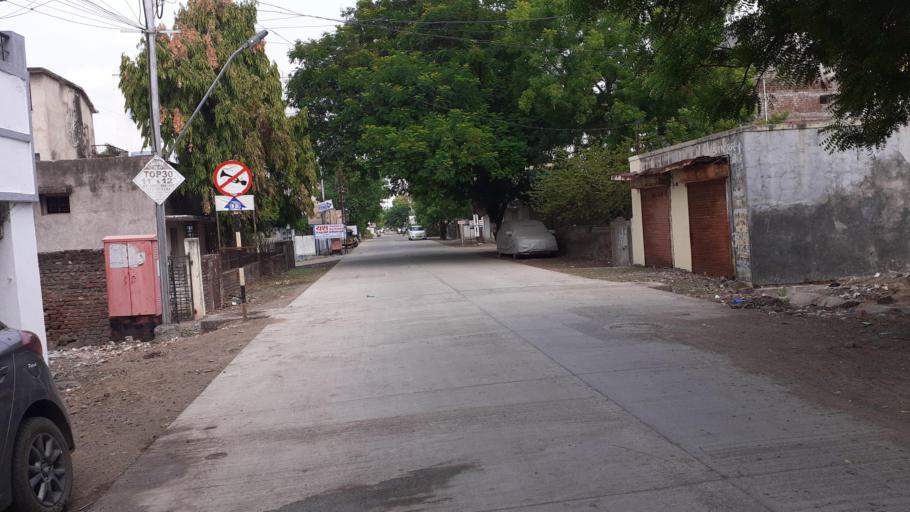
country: IN
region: Maharashtra
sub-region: Amravati Division
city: Amravati
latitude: 20.9343
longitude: 77.7700
